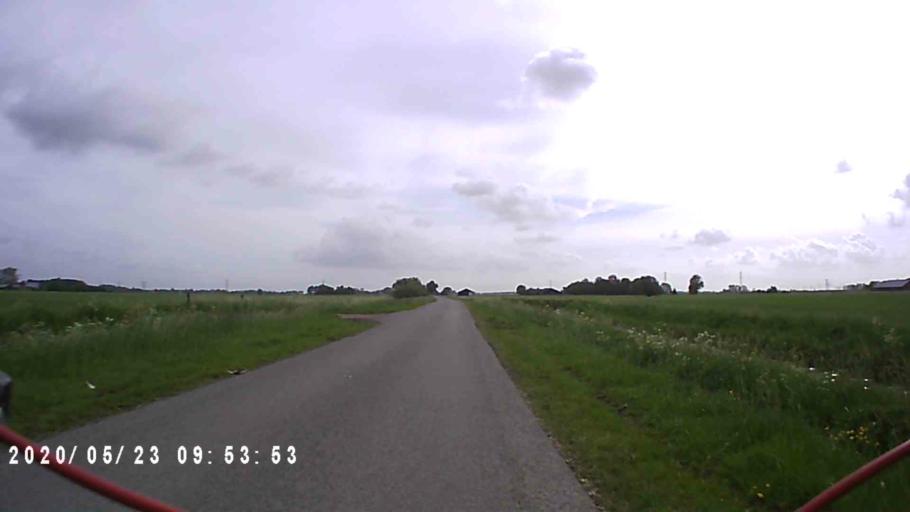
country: NL
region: Groningen
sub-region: Gemeente Appingedam
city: Appingedam
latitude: 53.3005
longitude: 6.7949
